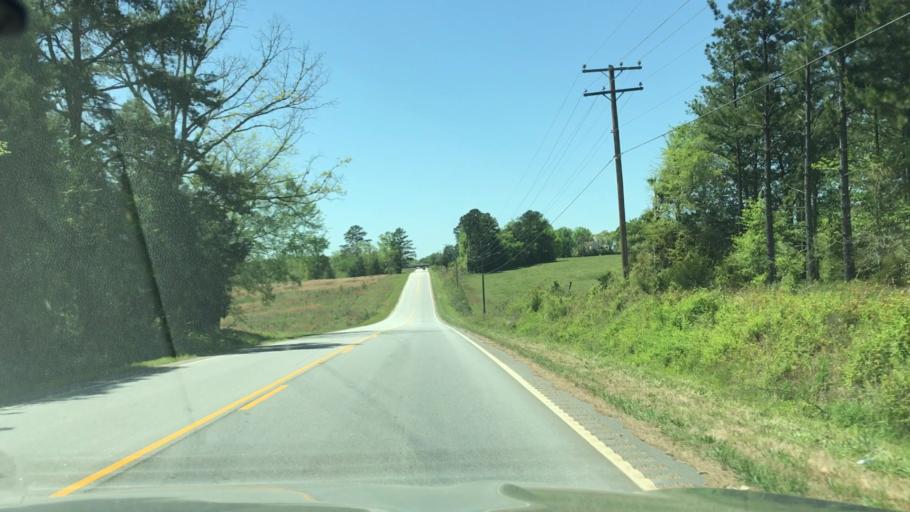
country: US
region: South Carolina
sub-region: Union County
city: Buffalo
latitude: 34.6835
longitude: -81.7160
